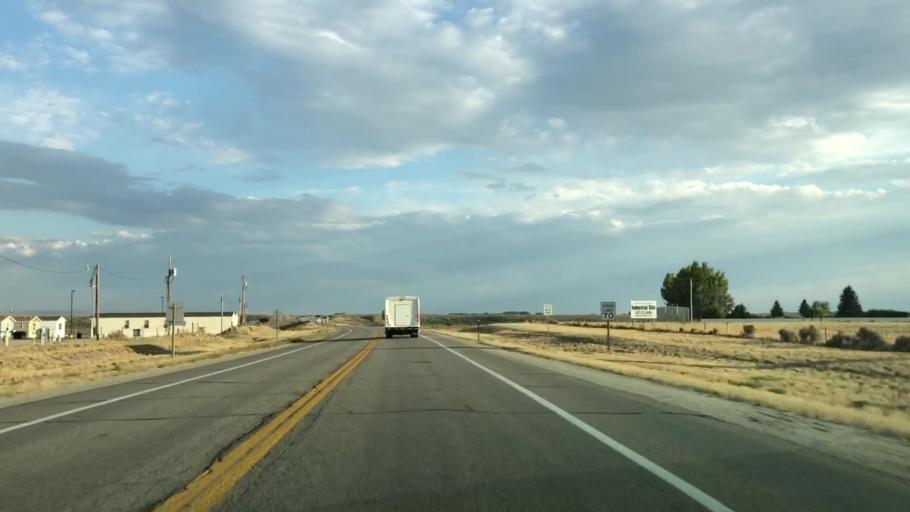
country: US
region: Wyoming
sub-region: Sweetwater County
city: North Rock Springs
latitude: 42.1058
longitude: -109.4482
